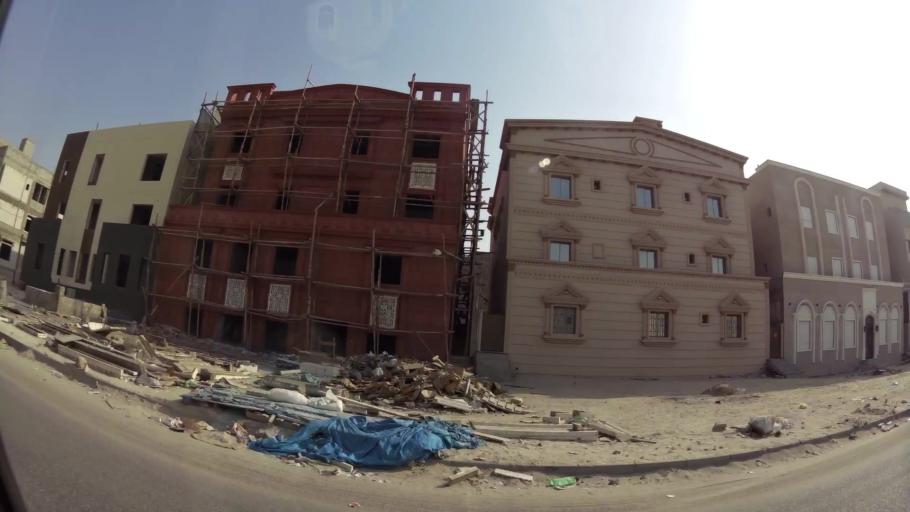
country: KW
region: Muhafazat al Jahra'
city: Al Jahra'
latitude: 29.3453
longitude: 47.7472
